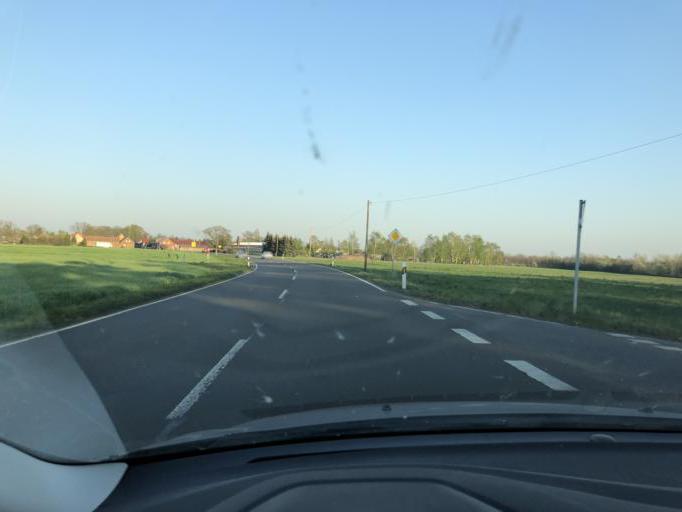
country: DE
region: Brandenburg
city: Welzow
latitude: 51.5266
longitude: 14.2152
